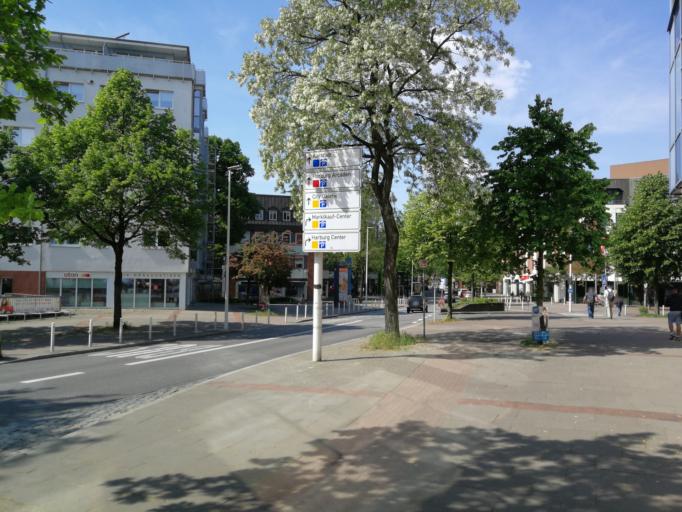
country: DE
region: Hamburg
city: Harburg
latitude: 53.4581
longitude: 9.9846
